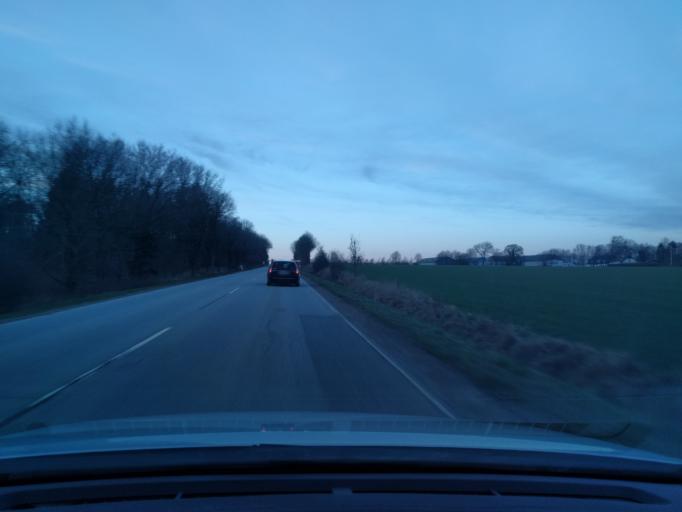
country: DK
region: South Denmark
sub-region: Haderslev Kommune
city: Gram
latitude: 55.3104
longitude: 9.1397
